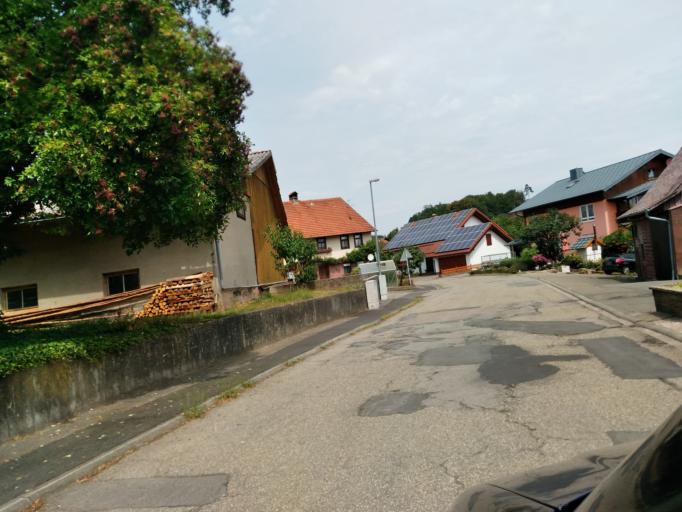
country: DE
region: Baden-Wuerttemberg
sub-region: Karlsruhe Region
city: Limbach
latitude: 49.4751
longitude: 9.1748
